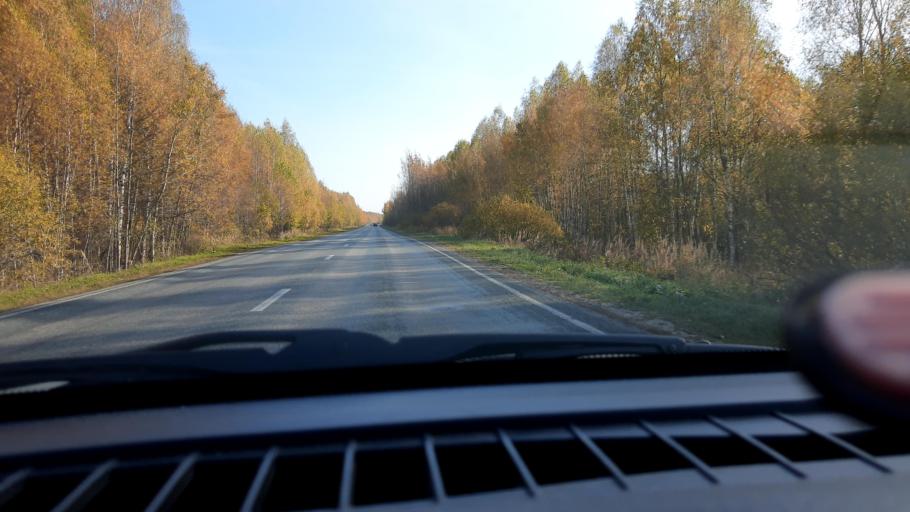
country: RU
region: Nizjnij Novgorod
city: Neklyudovo
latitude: 56.5281
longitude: 43.8186
